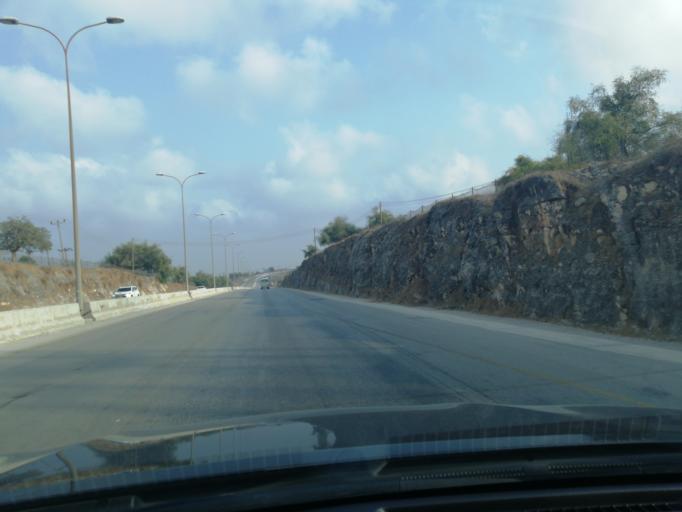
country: OM
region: Zufar
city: Salalah
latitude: 17.1855
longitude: 54.1191
